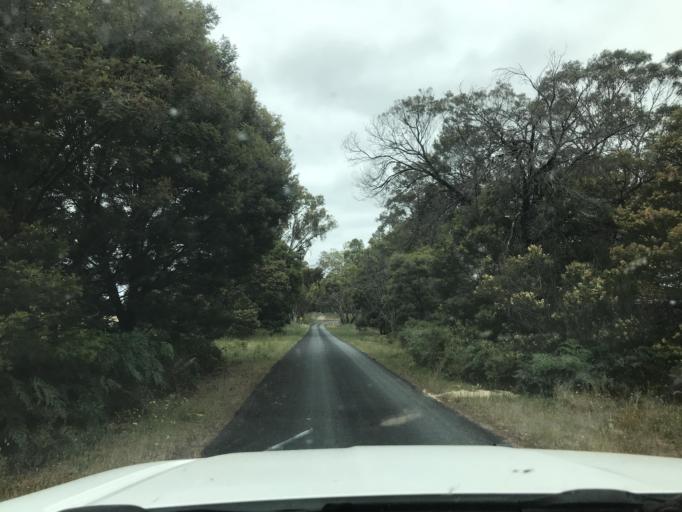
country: AU
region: South Australia
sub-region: Wattle Range
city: Penola
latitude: -37.2022
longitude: 140.9715
